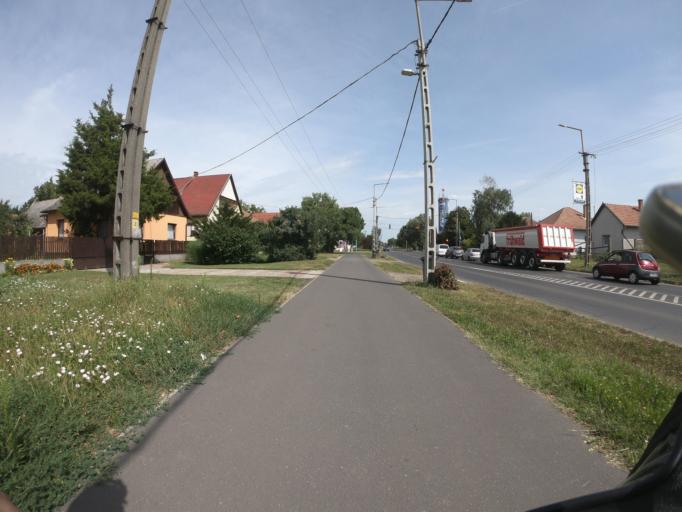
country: HU
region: Jasz-Nagykun-Szolnok
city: Tiszafured
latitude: 47.6174
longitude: 20.7482
